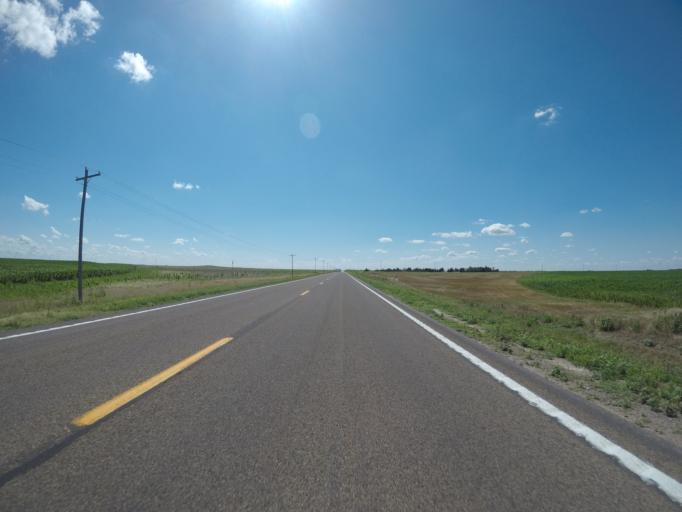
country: US
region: Nebraska
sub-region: Chase County
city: Imperial
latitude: 40.5377
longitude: -101.6816
